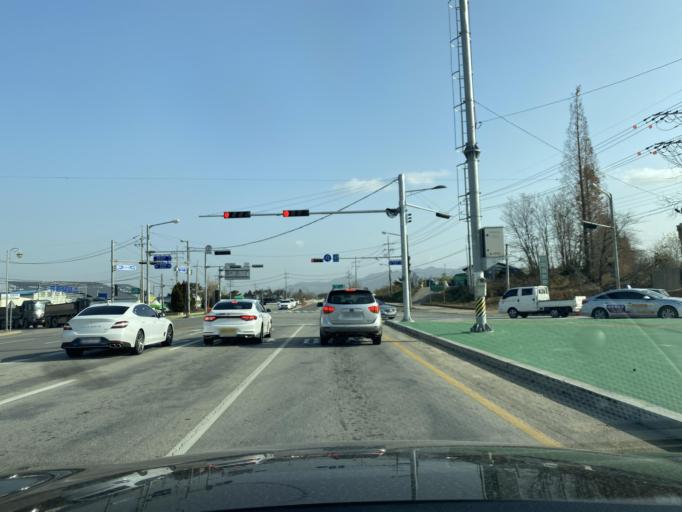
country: KR
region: Chungcheongnam-do
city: Yesan
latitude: 36.6869
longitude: 126.7835
